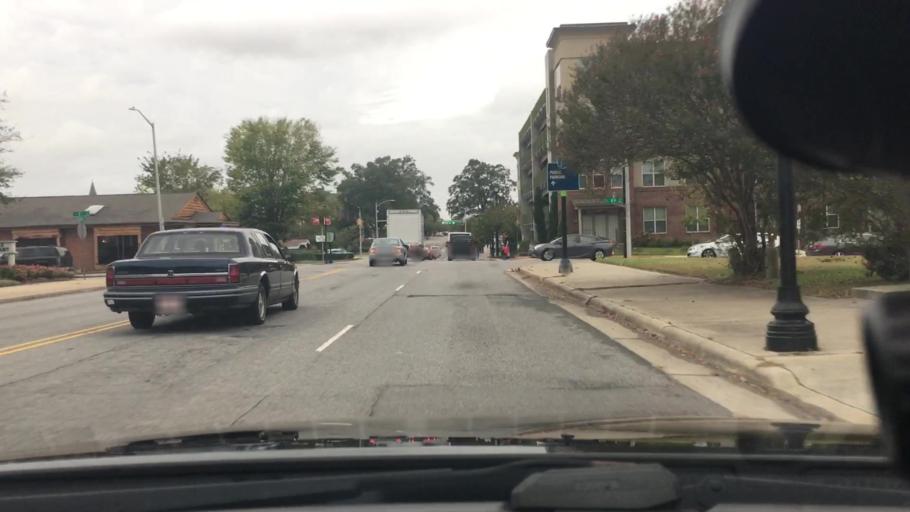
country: US
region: North Carolina
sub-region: Pitt County
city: Greenville
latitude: 35.6078
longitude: -77.3739
